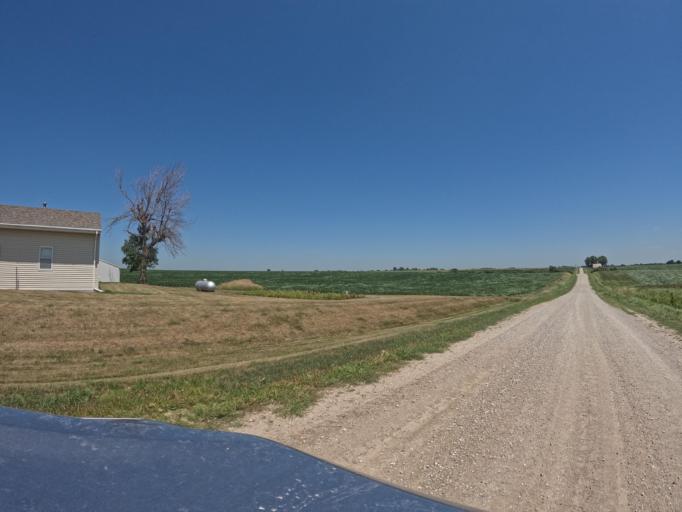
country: US
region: Iowa
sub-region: Keokuk County
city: Sigourney
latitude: 41.4235
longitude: -92.3288
